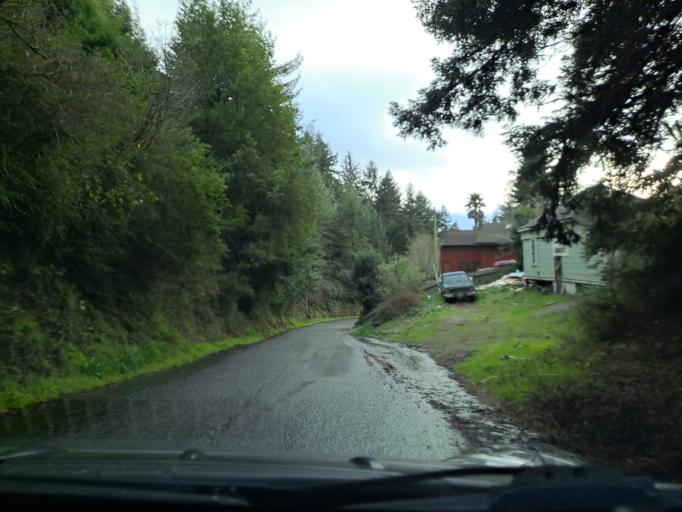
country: US
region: California
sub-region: Humboldt County
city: Fortuna
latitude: 40.6049
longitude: -124.1557
